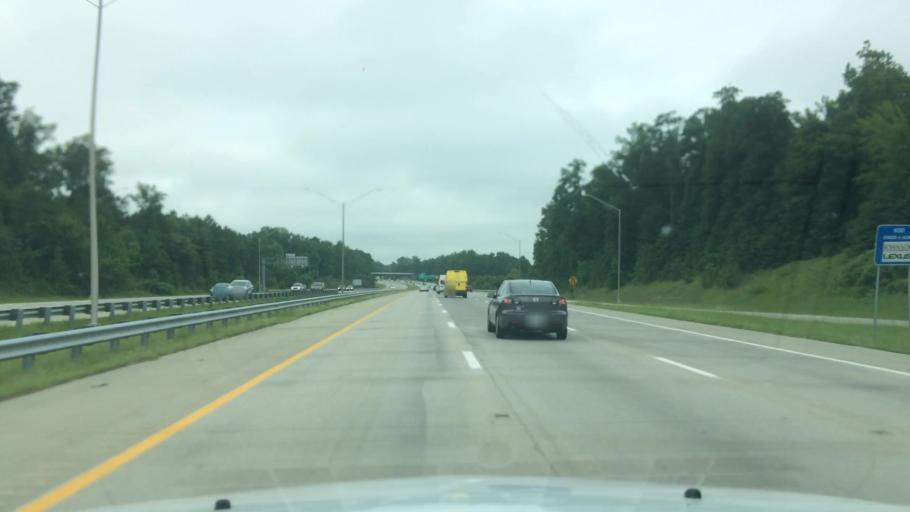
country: US
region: North Carolina
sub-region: Wake County
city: Knightdale
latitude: 35.8641
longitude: -78.5510
